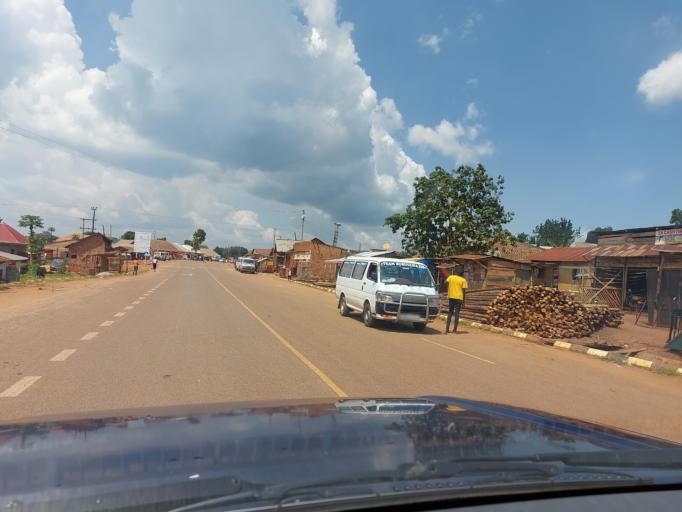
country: UG
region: Central Region
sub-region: Buikwe District
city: Buikwe
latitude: 0.3112
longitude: 33.1015
